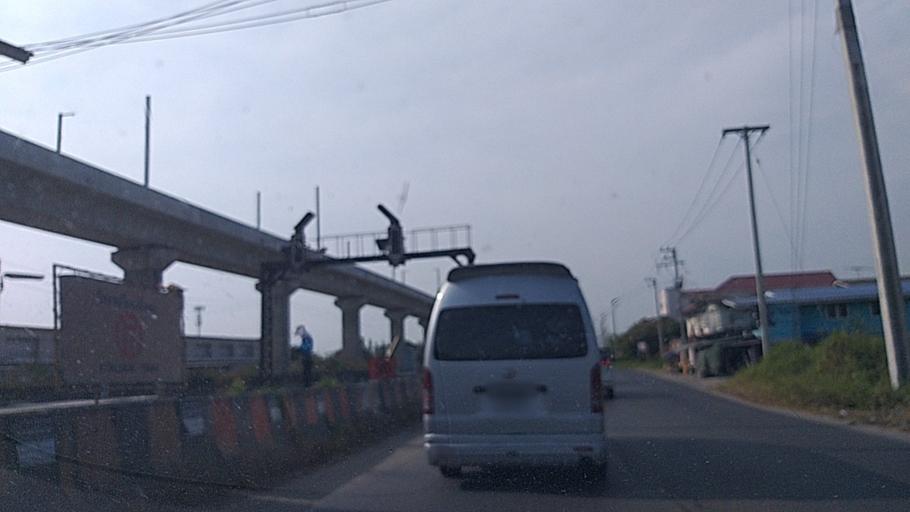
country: TH
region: Phra Nakhon Si Ayutthaya
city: Ban Bang Kadi Pathum Thani
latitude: 13.9857
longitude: 100.6024
